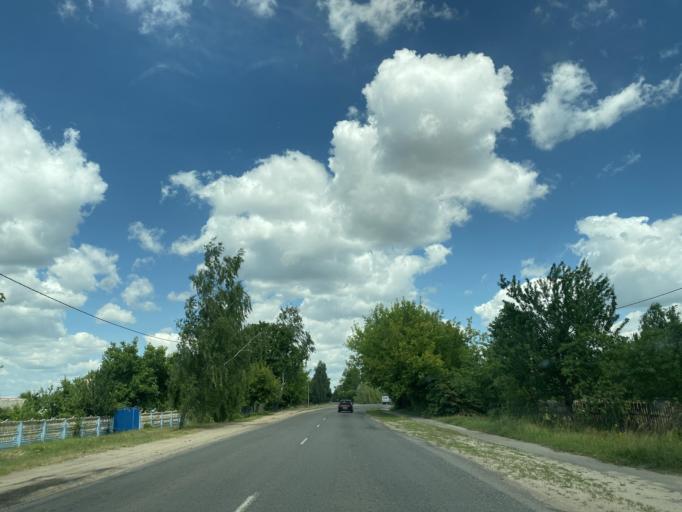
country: BY
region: Brest
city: Ivanava
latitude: 52.1634
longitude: 25.5473
